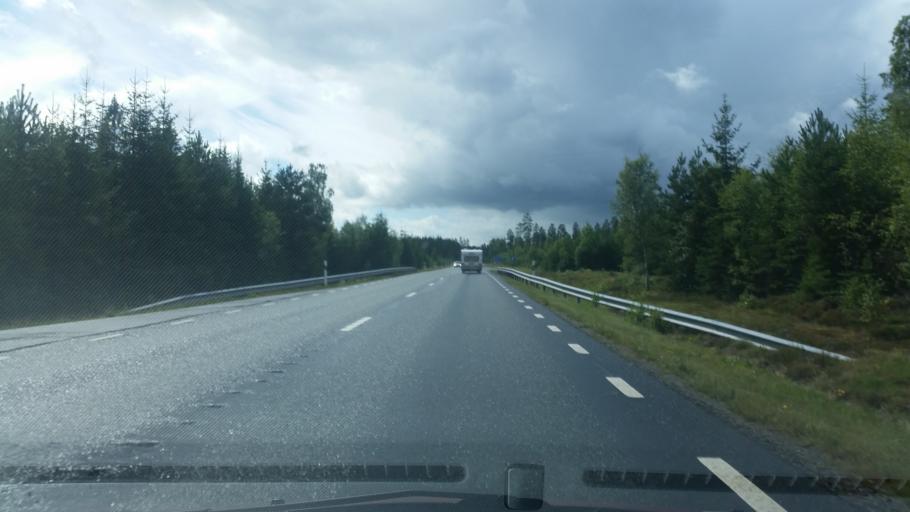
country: SE
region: Joenkoeping
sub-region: Gislaveds Kommun
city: Gislaved
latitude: 57.3674
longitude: 13.5717
